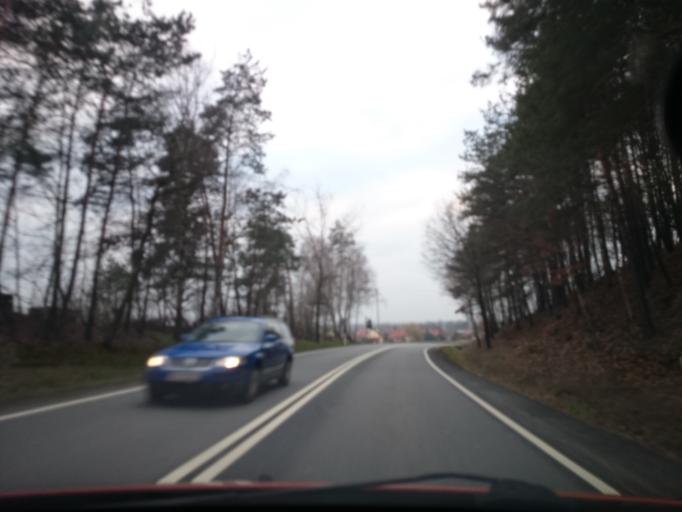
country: PL
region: Opole Voivodeship
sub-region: Powiat nyski
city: Sidzina
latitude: 50.5881
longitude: 17.4954
